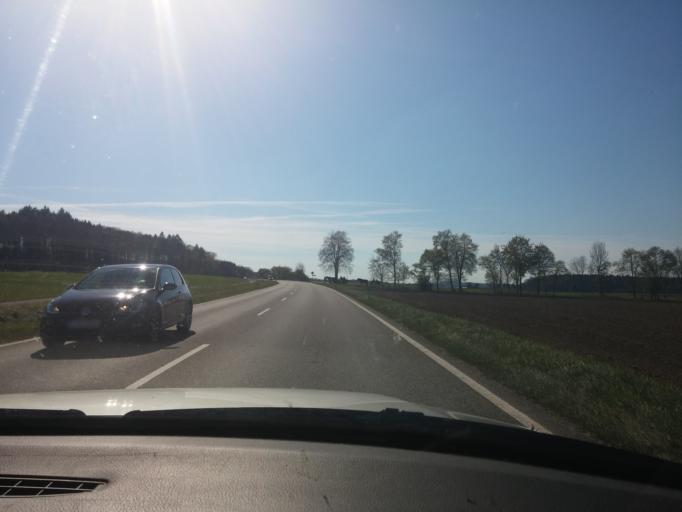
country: DE
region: Baden-Wuerttemberg
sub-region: Tuebingen Region
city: Bad Schussenried
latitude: 48.0251
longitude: 9.6889
